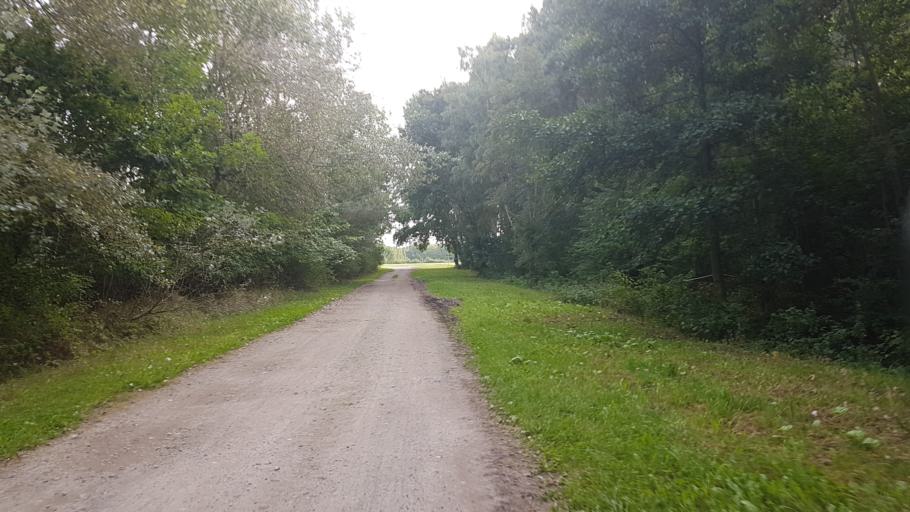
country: DE
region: Mecklenburg-Vorpommern
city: Gingst
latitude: 54.4767
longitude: 13.1603
